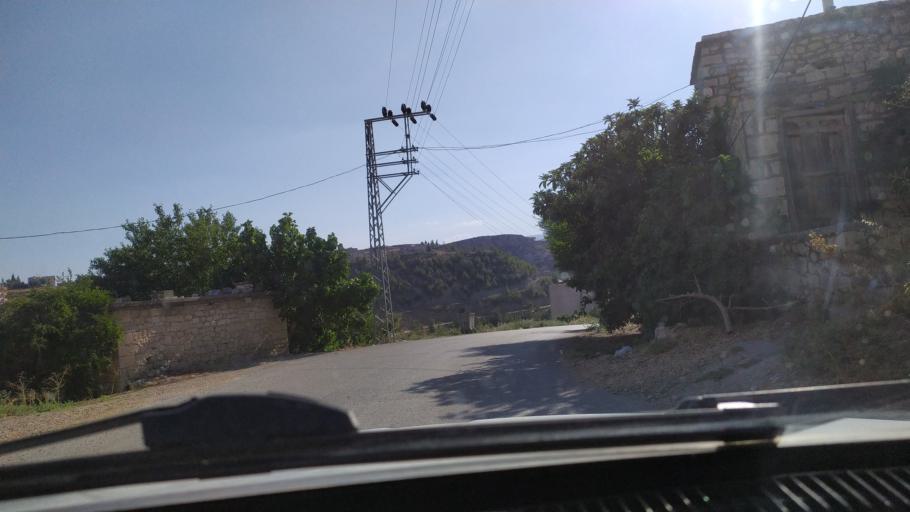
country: TR
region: Mersin
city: Mut
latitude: 36.6466
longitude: 33.4309
